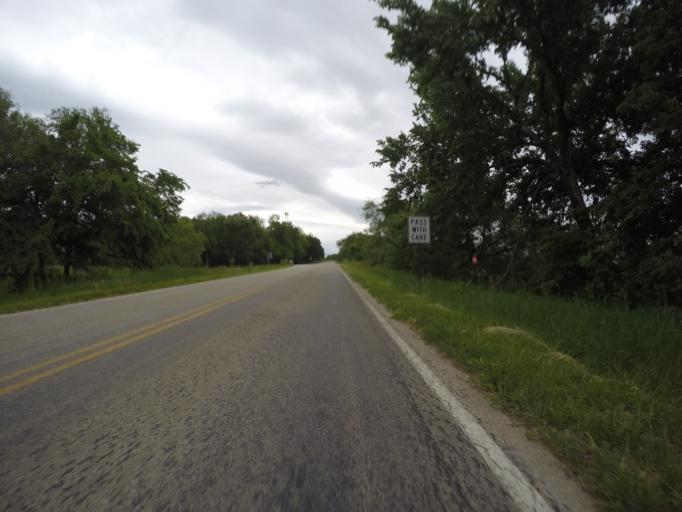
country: US
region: Kansas
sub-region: Pottawatomie County
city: Wamego
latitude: 39.1812
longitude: -96.3900
